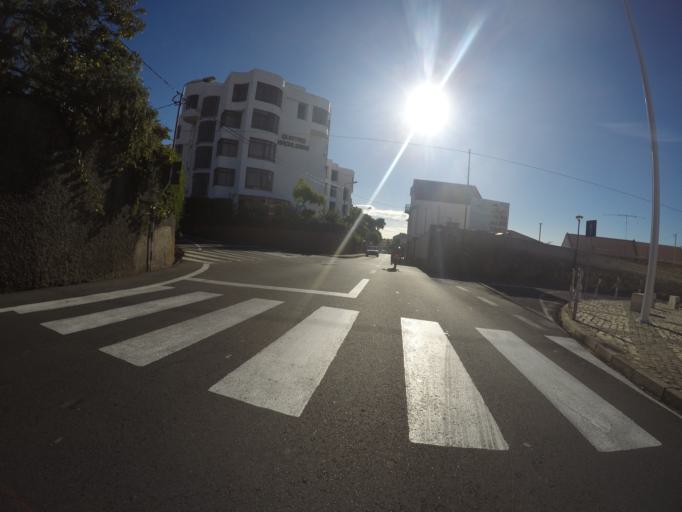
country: PT
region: Madeira
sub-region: Funchal
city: Nossa Senhora do Monte
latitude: 32.6573
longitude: -16.9275
